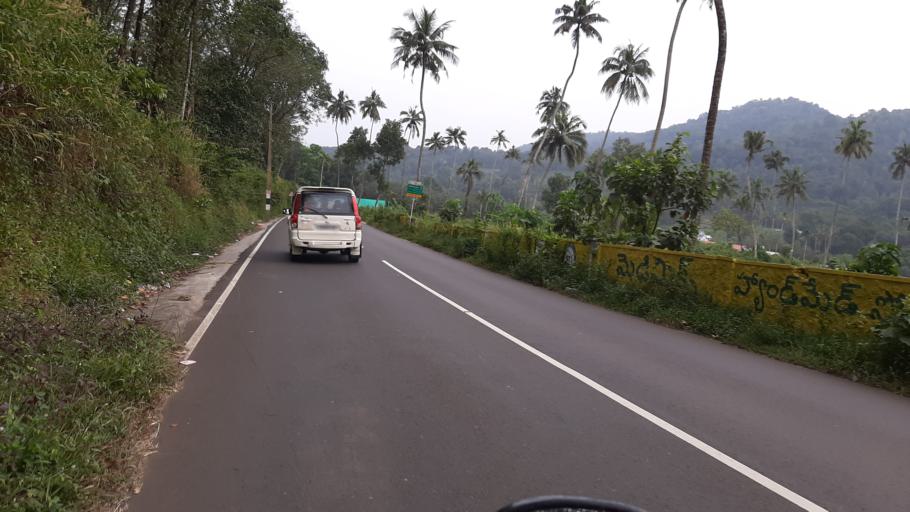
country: IN
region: Kerala
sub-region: Pattanamtitta
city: Pathanamthitta
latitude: 9.4530
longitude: 76.8685
